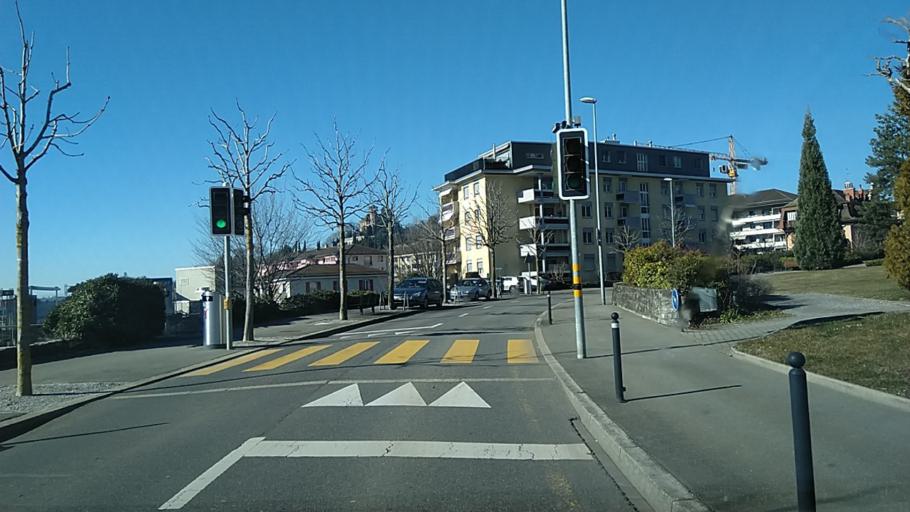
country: CH
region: Vaud
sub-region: Riviera-Pays-d'Enhaut District
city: Le Chatelard
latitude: 46.4428
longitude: 6.8975
